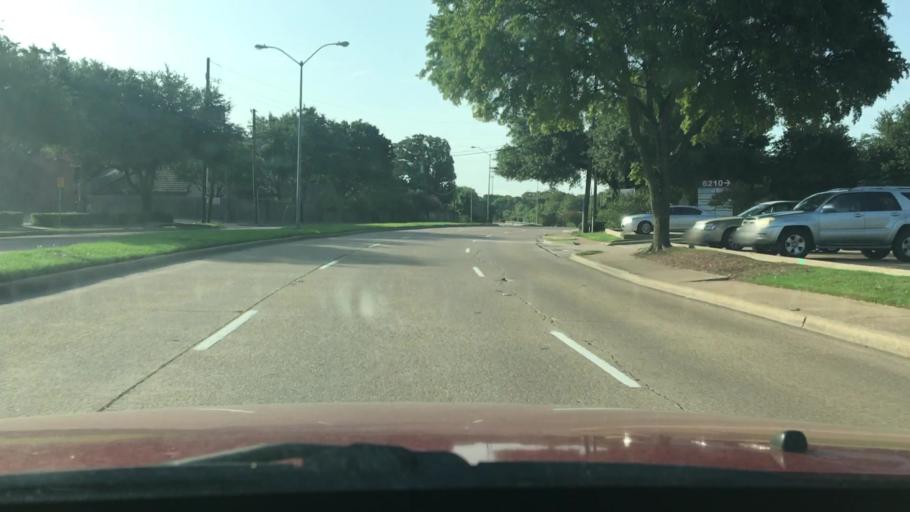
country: US
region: Texas
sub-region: Dallas County
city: Addison
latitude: 32.9826
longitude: -96.8014
